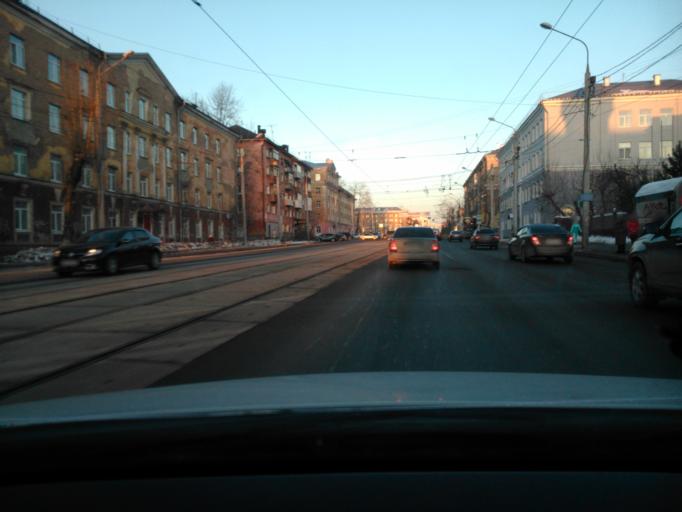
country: RU
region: Perm
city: Perm
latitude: 57.9940
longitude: 56.2485
